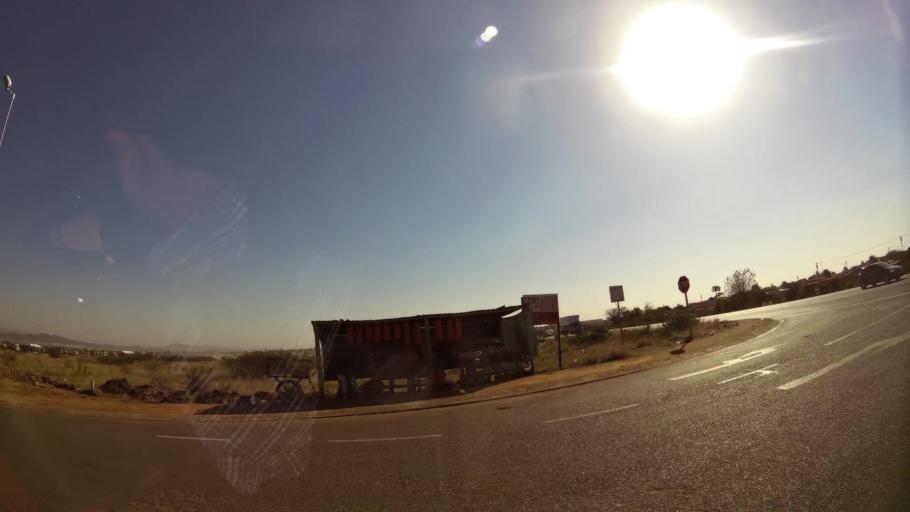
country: ZA
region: Gauteng
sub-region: City of Tshwane Metropolitan Municipality
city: Mabopane
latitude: -25.5542
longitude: 28.0955
